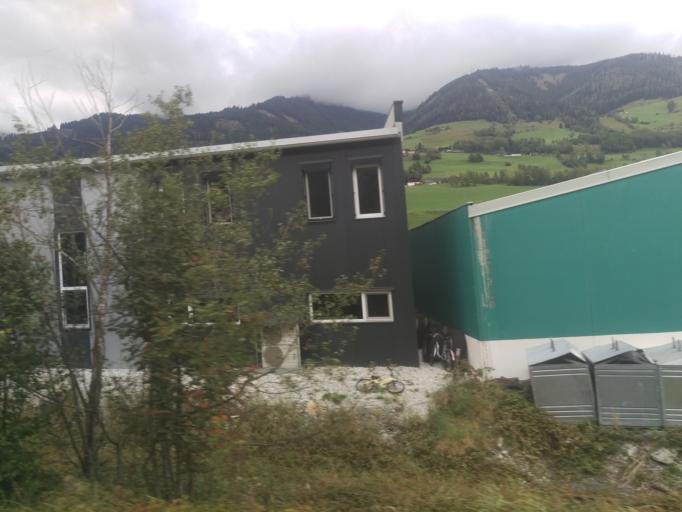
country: AT
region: Salzburg
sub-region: Politischer Bezirk Zell am See
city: Uttendorf
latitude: 47.2814
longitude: 12.5866
